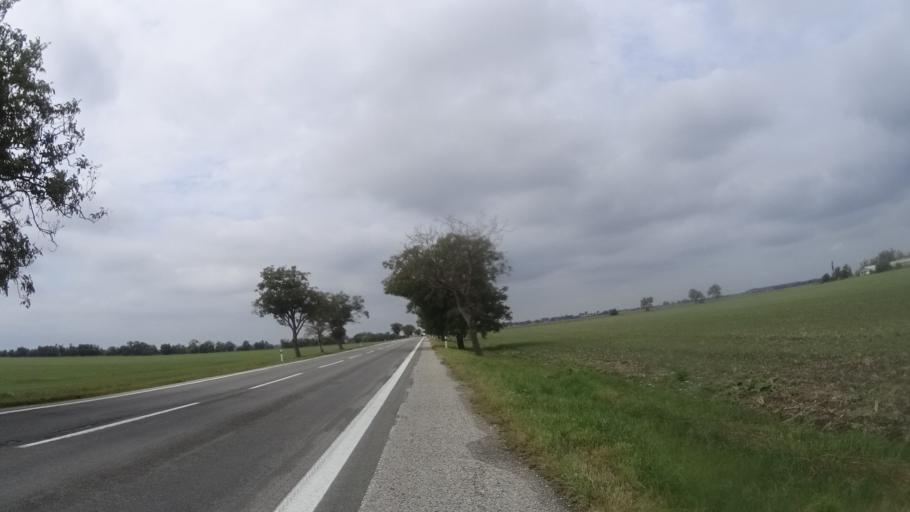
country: HU
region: Komarom-Esztergom
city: Acs
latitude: 47.7666
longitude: 18.0028
